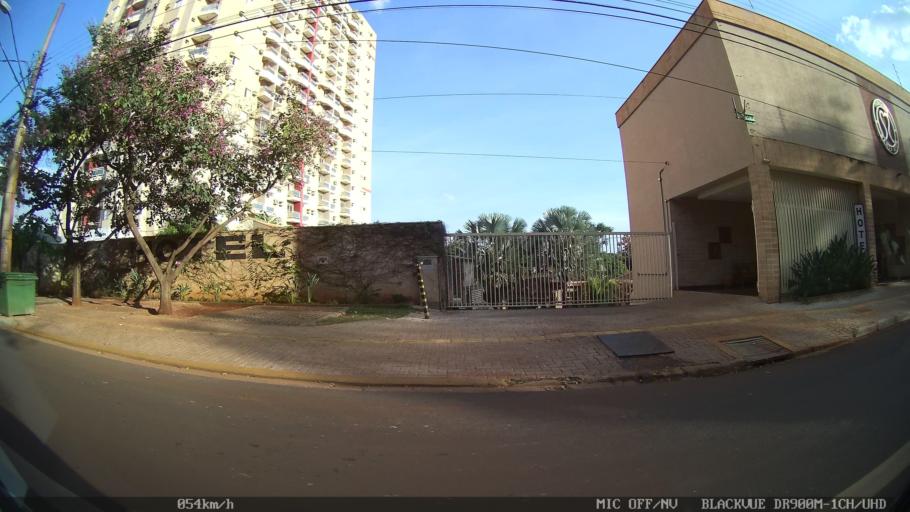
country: BR
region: Sao Paulo
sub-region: Ribeirao Preto
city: Ribeirao Preto
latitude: -21.1745
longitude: -47.8401
